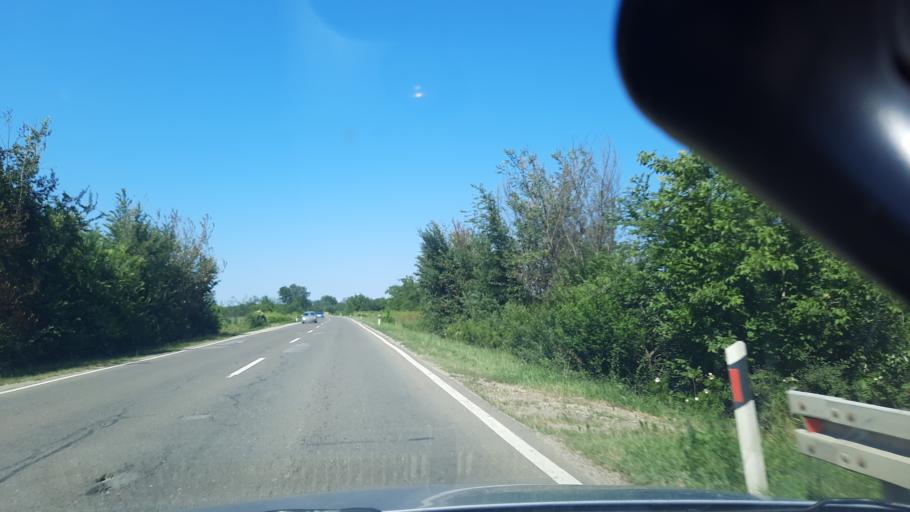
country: RS
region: Central Serbia
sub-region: Branicevski Okrug
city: Pozarevac
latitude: 44.6111
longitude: 21.1428
